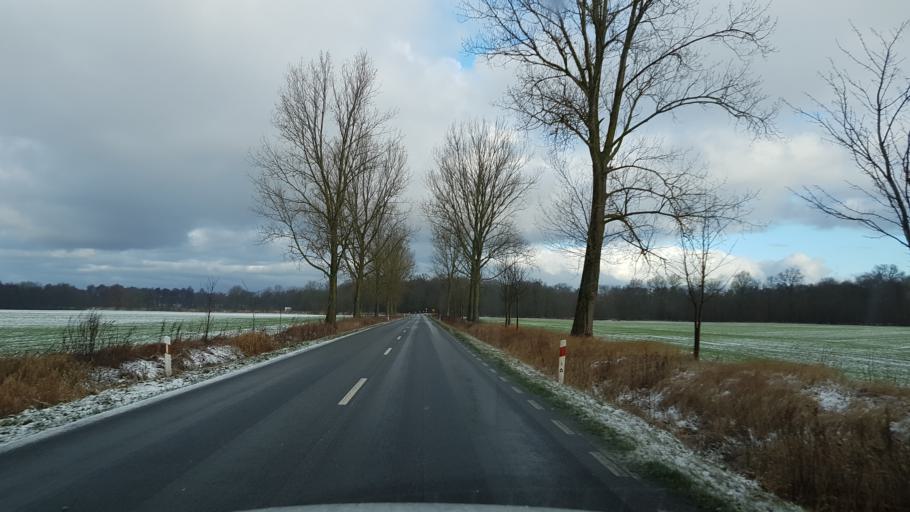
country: PL
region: West Pomeranian Voivodeship
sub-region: Powiat gryficki
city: Karnice
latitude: 54.0226
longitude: 15.0603
